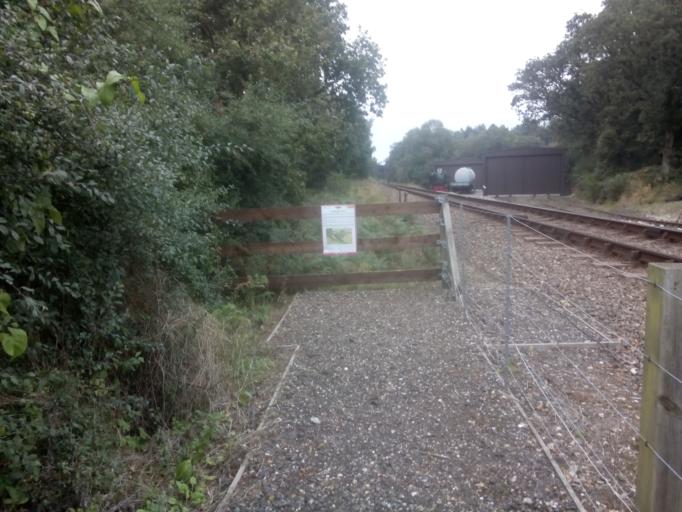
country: GB
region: England
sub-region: Norfolk
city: Briston
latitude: 52.9193
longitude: 1.1140
